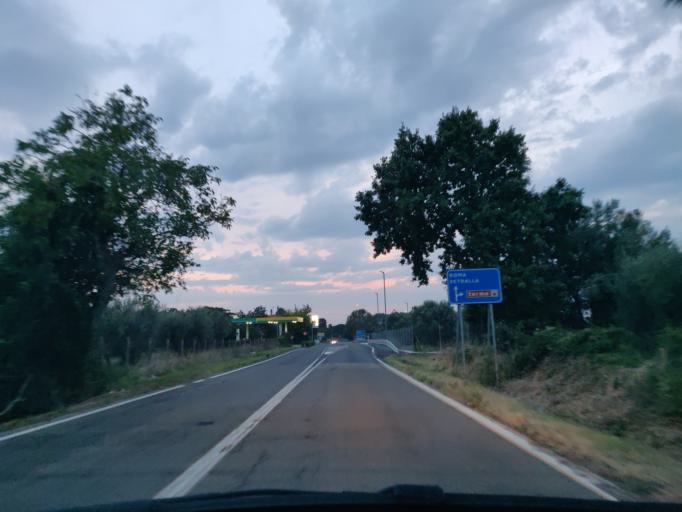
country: IT
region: Latium
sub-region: Provincia di Viterbo
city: Vetralla
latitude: 42.3736
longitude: 12.0633
